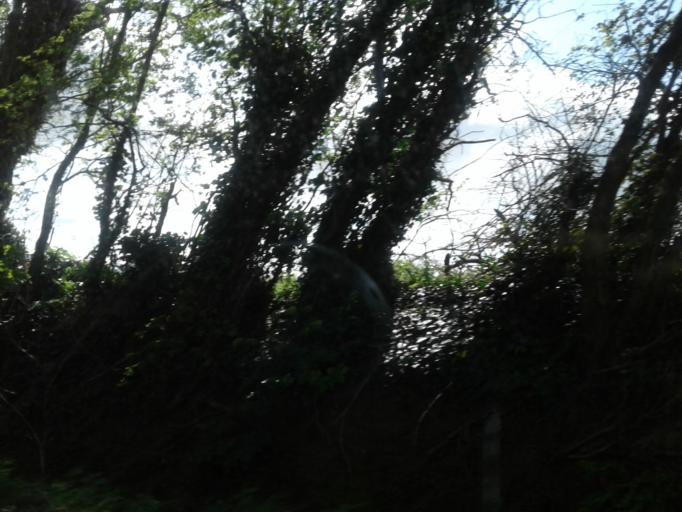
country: IE
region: Leinster
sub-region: An Mhi
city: Ashbourne
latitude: 53.4890
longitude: -6.3121
